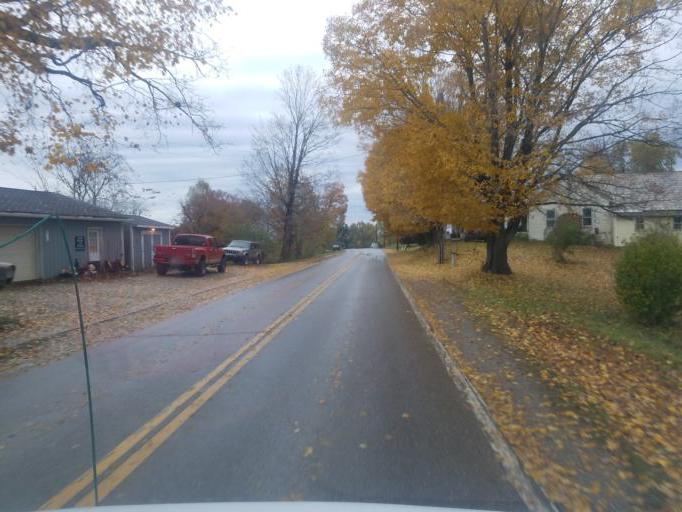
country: US
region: Ohio
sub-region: Morgan County
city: McConnelsville
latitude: 39.4933
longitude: -81.8650
